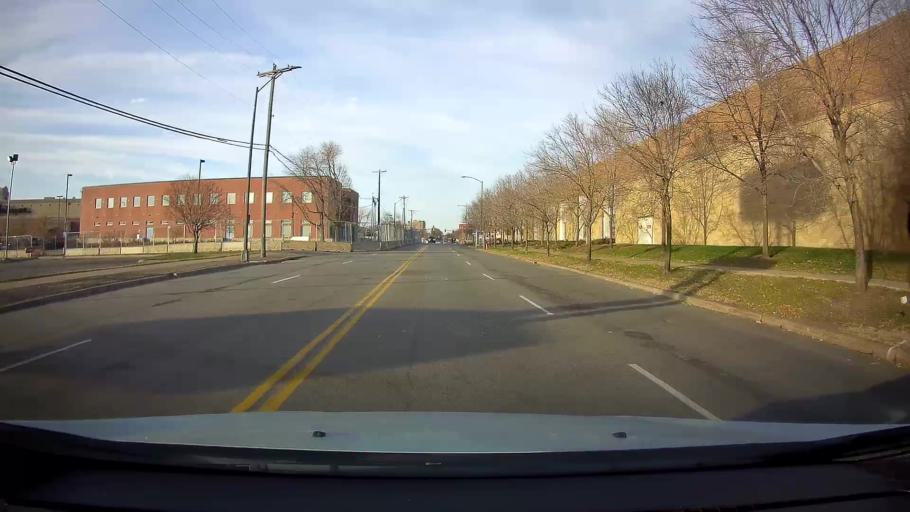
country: US
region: Minnesota
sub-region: Ramsey County
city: Falcon Heights
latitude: 44.9524
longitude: -93.1568
